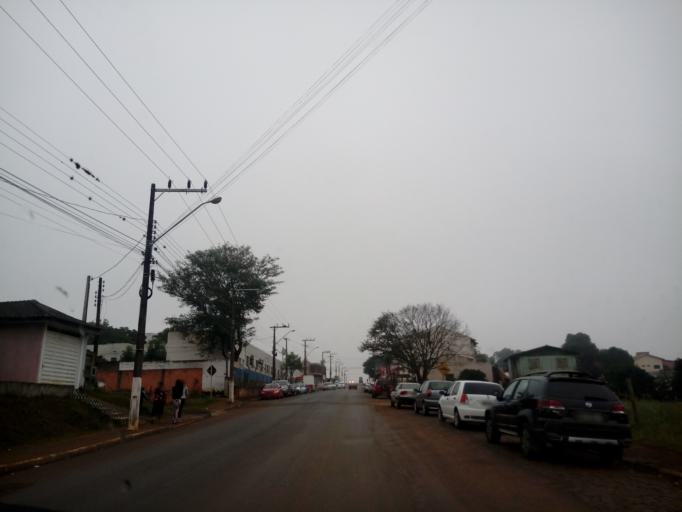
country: BR
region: Santa Catarina
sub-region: Chapeco
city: Chapeco
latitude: -27.1017
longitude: -52.6736
